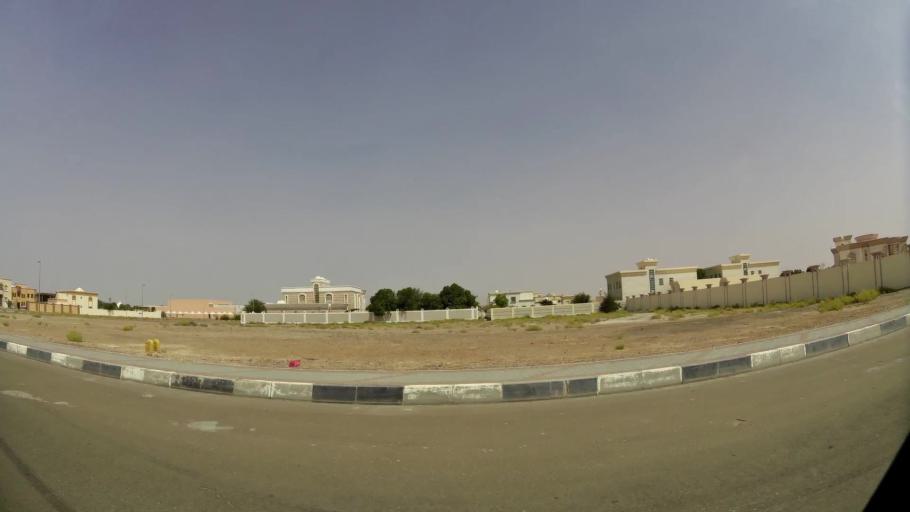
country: AE
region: Abu Dhabi
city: Al Ain
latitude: 24.1612
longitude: 55.6598
